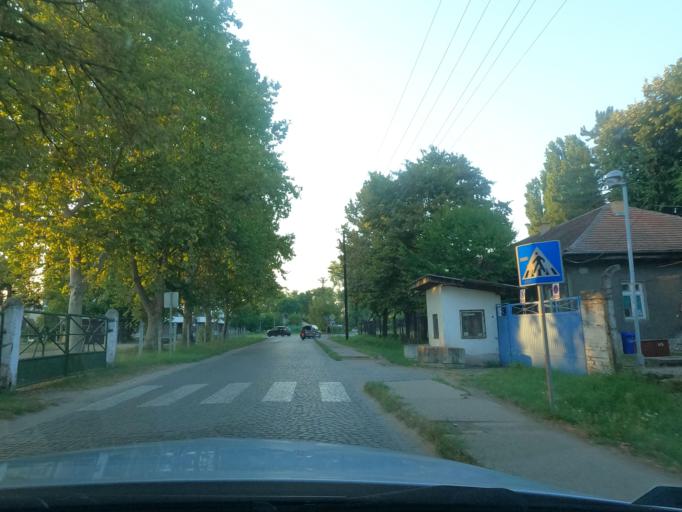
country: RS
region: Autonomna Pokrajina Vojvodina
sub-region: Juznobacki Okrug
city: Novi Sad
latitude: 45.2342
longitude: 19.8262
